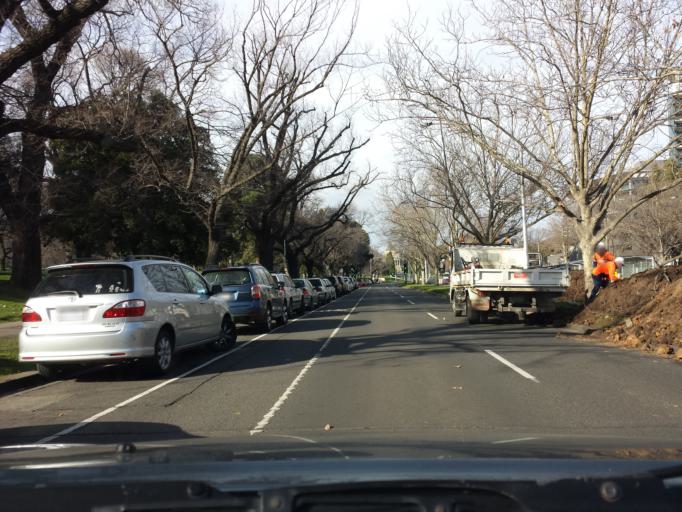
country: AU
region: Victoria
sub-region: Melbourne
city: Southbank
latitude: -37.8237
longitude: 144.9705
